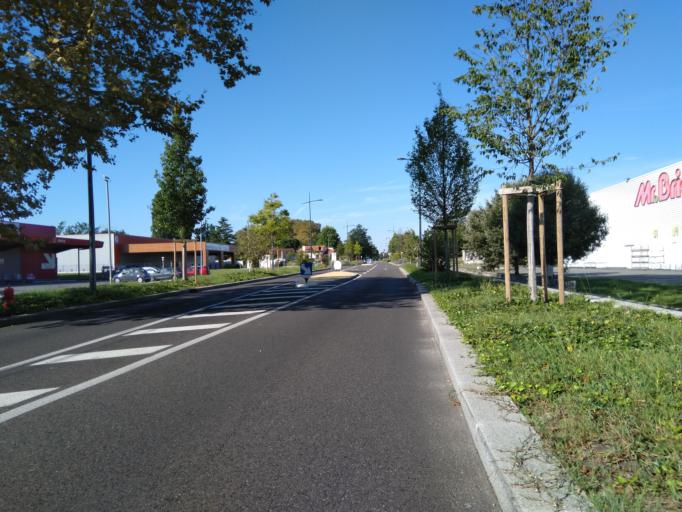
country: FR
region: Aquitaine
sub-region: Departement des Landes
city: Saint-Paul-les-Dax
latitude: 43.7285
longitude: -1.0408
